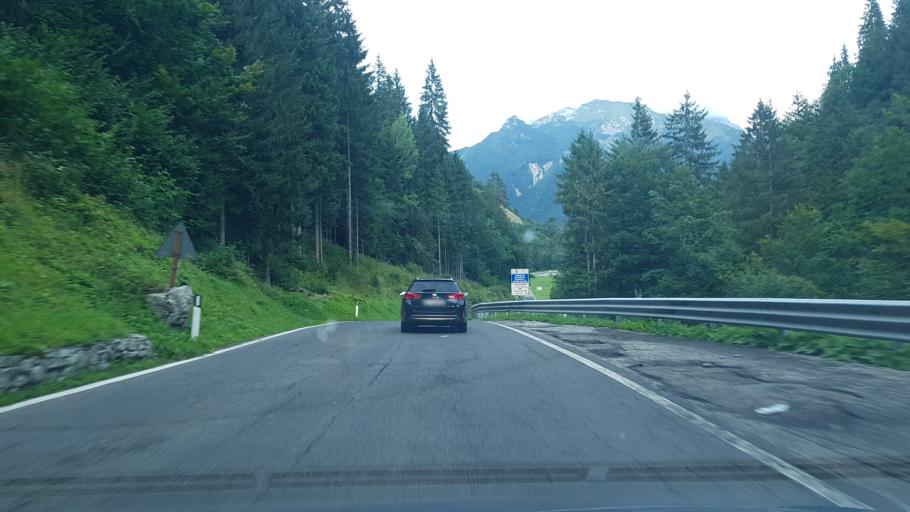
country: IT
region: Friuli Venezia Giulia
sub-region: Provincia di Udine
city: Forni Avoltri
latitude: 46.5690
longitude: 12.7381
